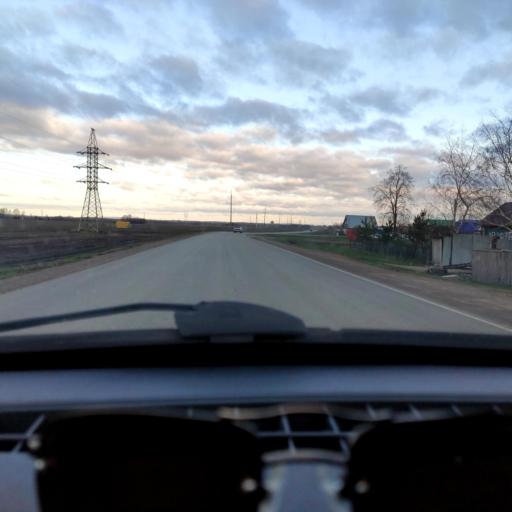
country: RU
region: Bashkortostan
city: Kabakovo
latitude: 54.5472
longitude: 56.0355
